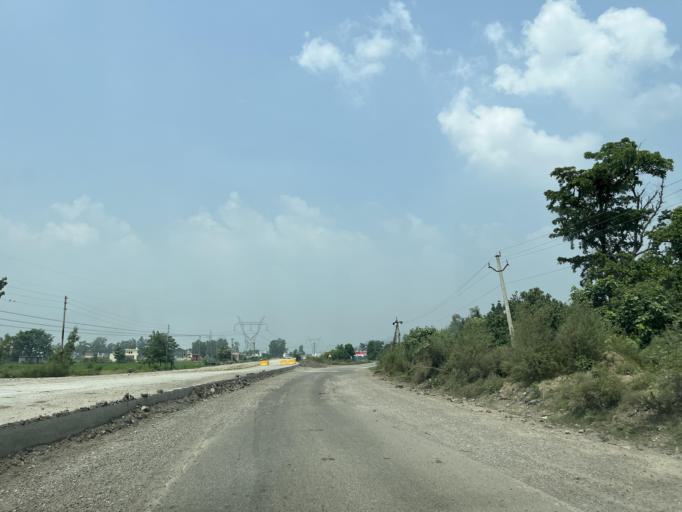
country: IN
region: Uttarakhand
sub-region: Haridwar
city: Haridwar
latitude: 29.8602
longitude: 78.1851
